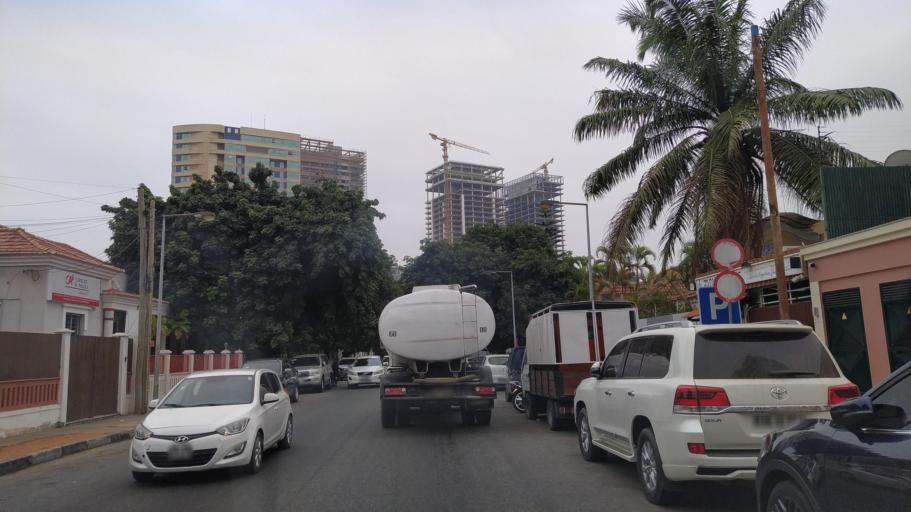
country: AO
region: Luanda
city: Luanda
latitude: -8.8190
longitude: 13.2371
